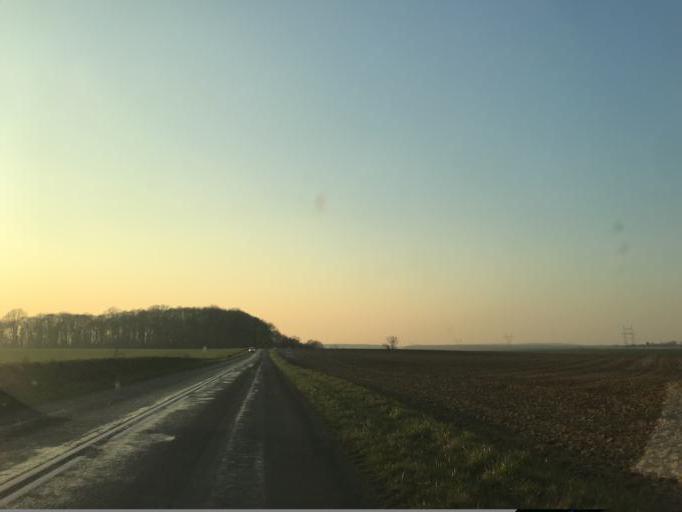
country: FR
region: Ile-de-France
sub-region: Departement de Seine-et-Marne
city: Charny
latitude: 49.0087
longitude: 2.7621
